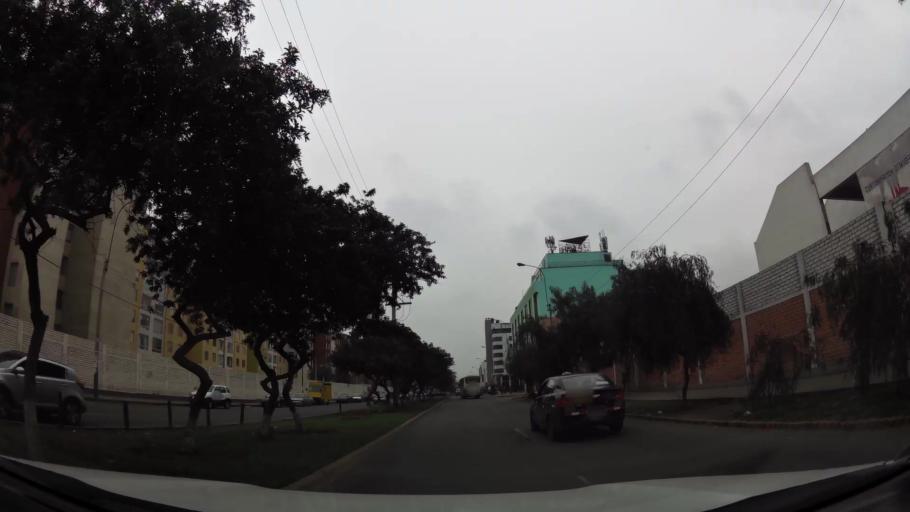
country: PE
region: Lima
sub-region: Lima
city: San Luis
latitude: -12.0782
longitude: -76.9992
